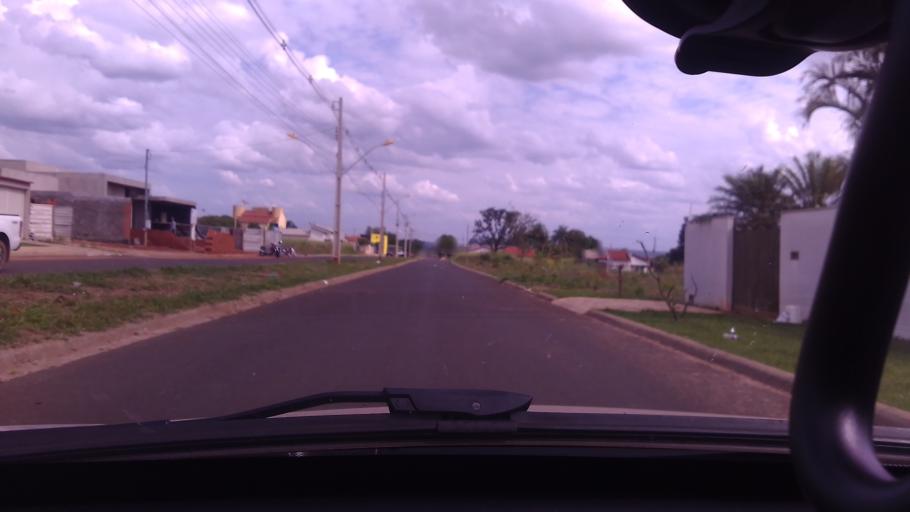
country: BR
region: Goias
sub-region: Mineiros
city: Mineiros
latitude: -17.5773
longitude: -52.5540
